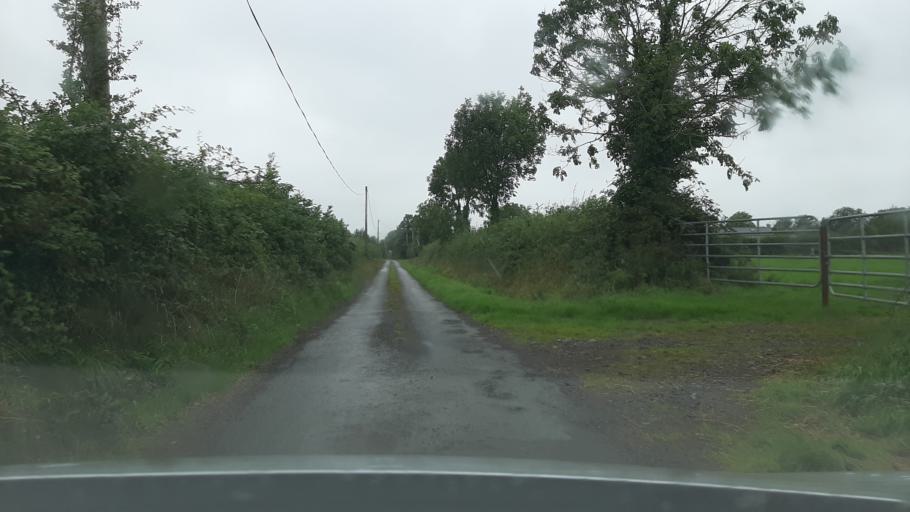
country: IE
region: Leinster
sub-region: Kildare
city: Rathangan
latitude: 53.1986
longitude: -7.0502
